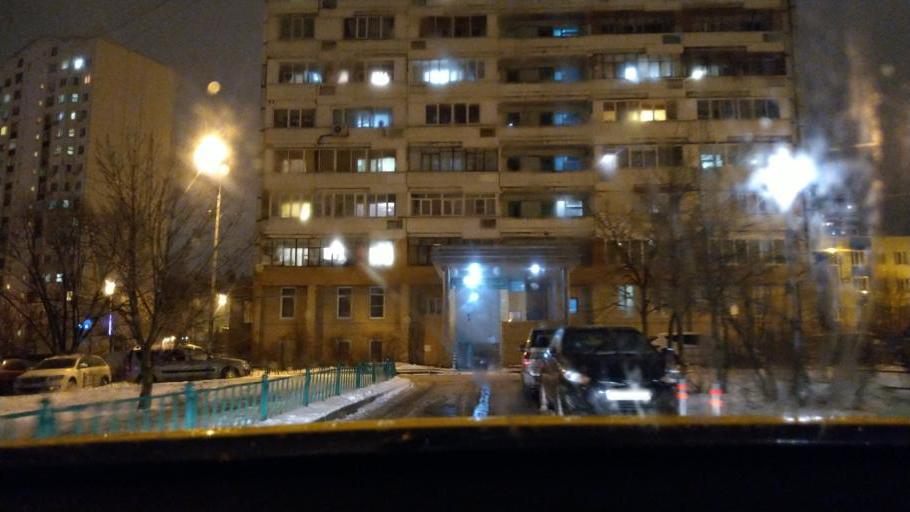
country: RU
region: Moskovskaya
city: Troitsk
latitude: 55.4911
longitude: 37.2975
